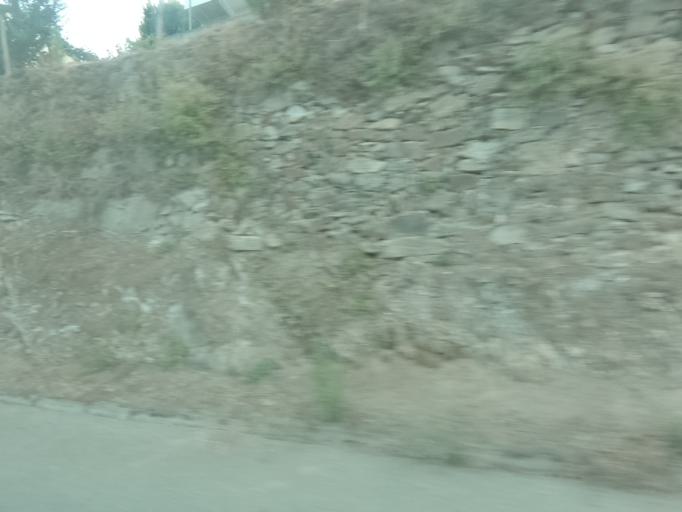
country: PT
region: Viseu
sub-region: Armamar
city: Armamar
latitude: 41.1292
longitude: -7.6974
